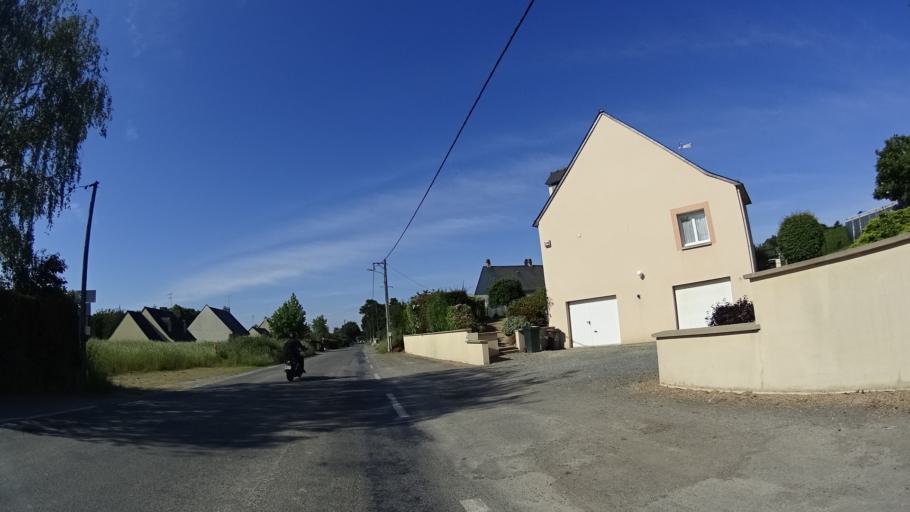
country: FR
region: Brittany
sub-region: Departement d'Ille-et-Vilaine
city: Guipry
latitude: 47.8213
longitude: -1.8449
